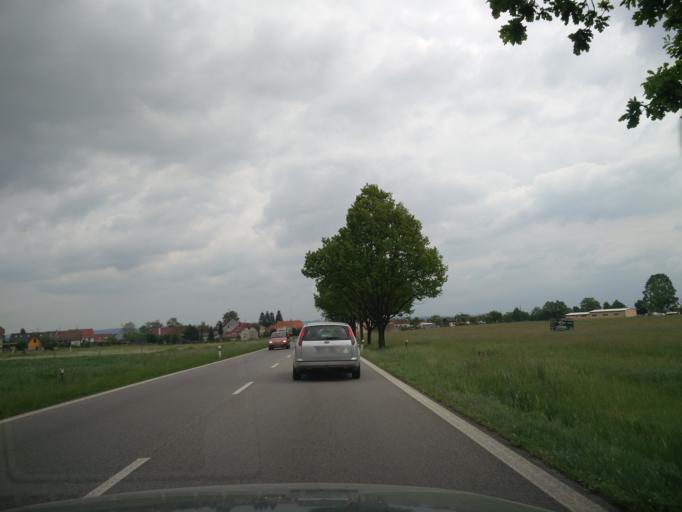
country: CZ
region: Jihocesky
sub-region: Okres Ceske Budejovice
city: Hluboka nad Vltavou
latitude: 49.0208
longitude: 14.4008
